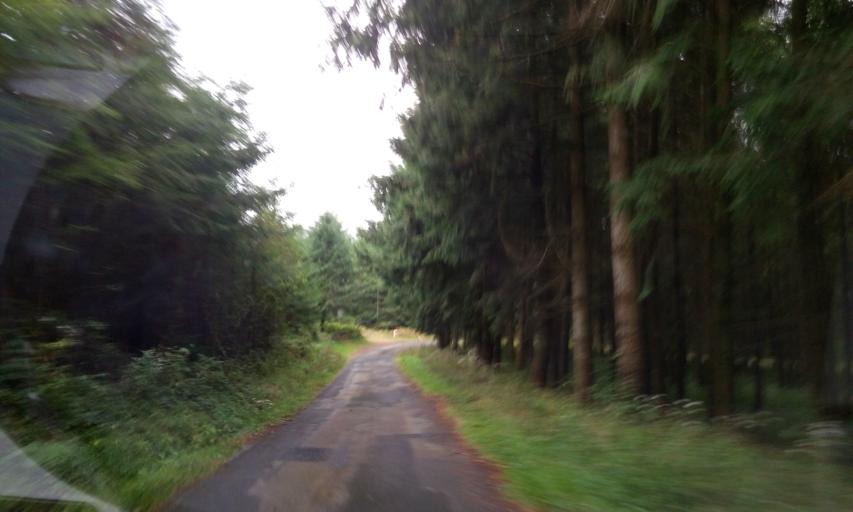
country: FR
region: Rhone-Alpes
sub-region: Departement du Rhone
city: Cublize
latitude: 45.9993
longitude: 4.4182
